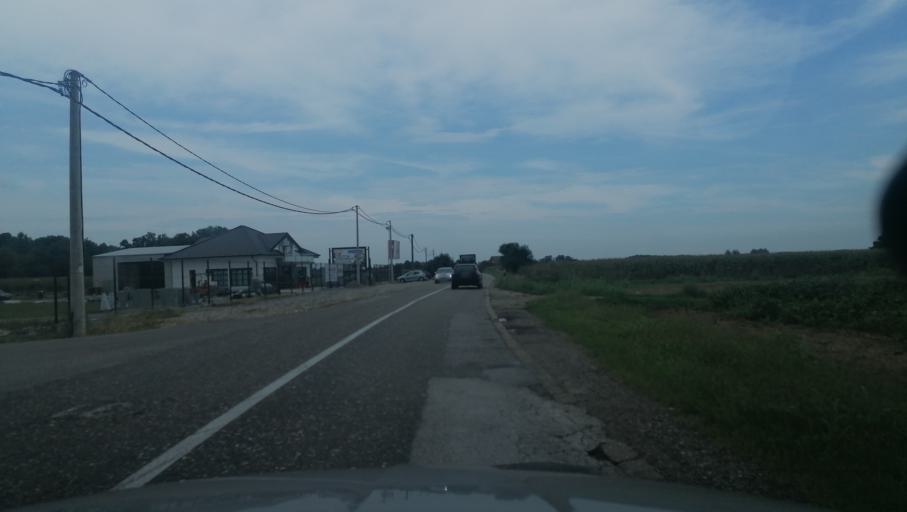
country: RS
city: Klenje
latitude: 44.8240
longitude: 19.4549
